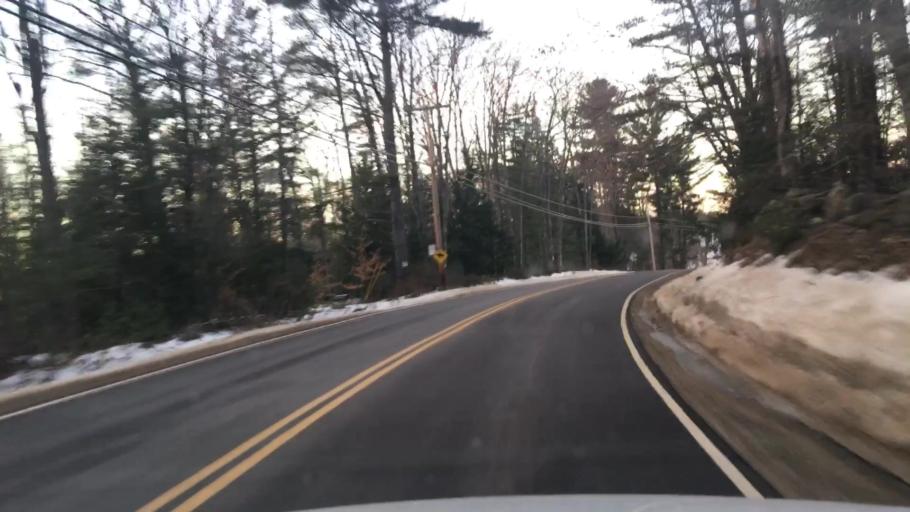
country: US
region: Maine
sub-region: York County
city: Lebanon
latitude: 43.4290
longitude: -70.8813
